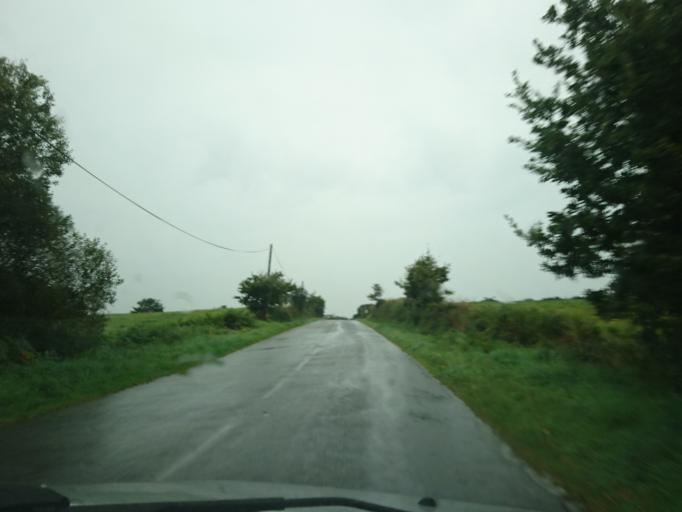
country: FR
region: Brittany
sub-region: Departement du Finistere
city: Le Drennec
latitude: 48.5369
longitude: -4.3754
